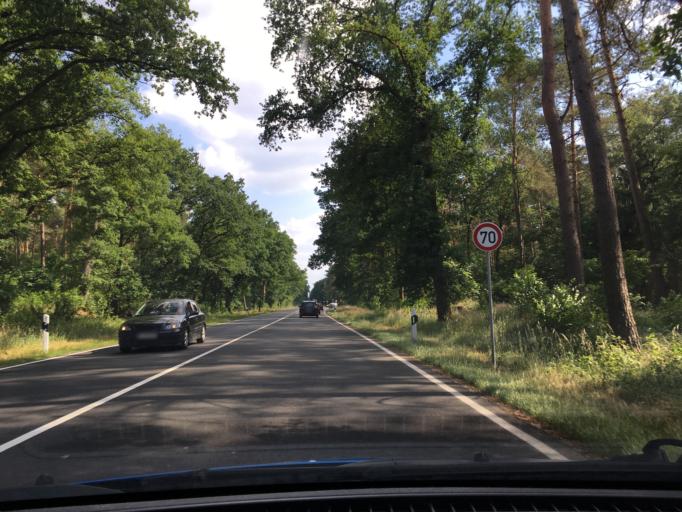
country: DE
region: Lower Saxony
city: Welle
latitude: 53.2046
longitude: 9.8237
